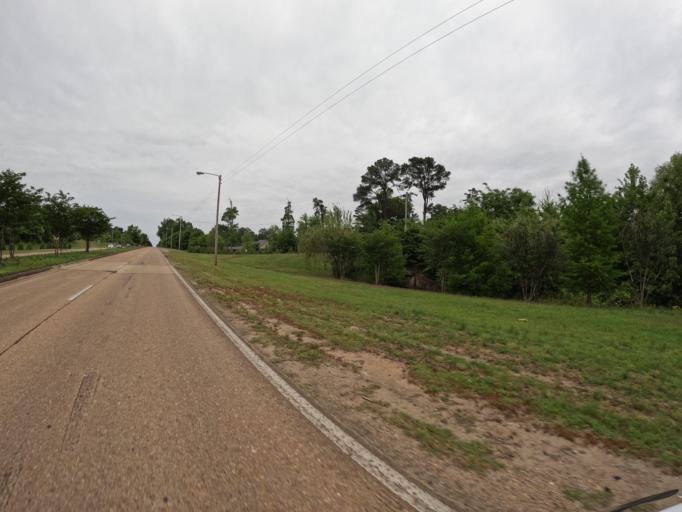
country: US
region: Mississippi
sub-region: Lee County
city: Tupelo
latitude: 34.2785
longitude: -88.7255
